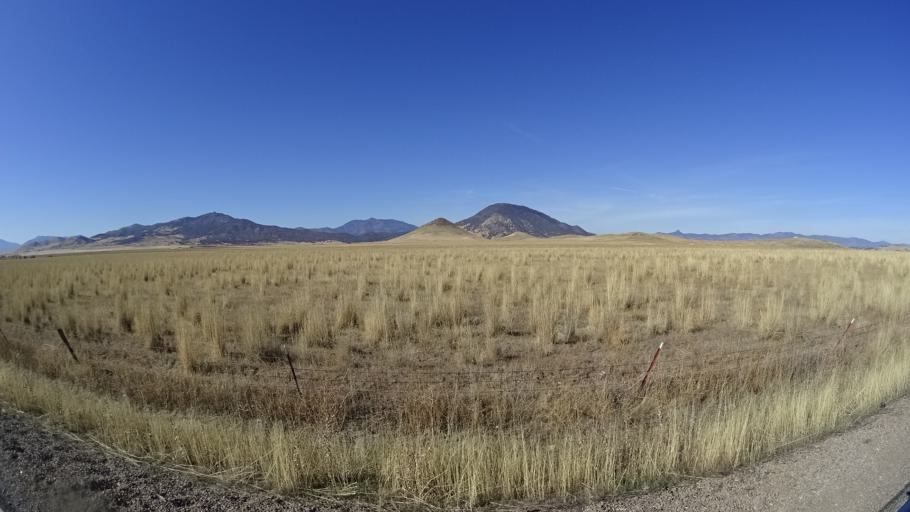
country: US
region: California
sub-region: Siskiyou County
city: Montague
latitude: 41.8037
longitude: -122.4449
